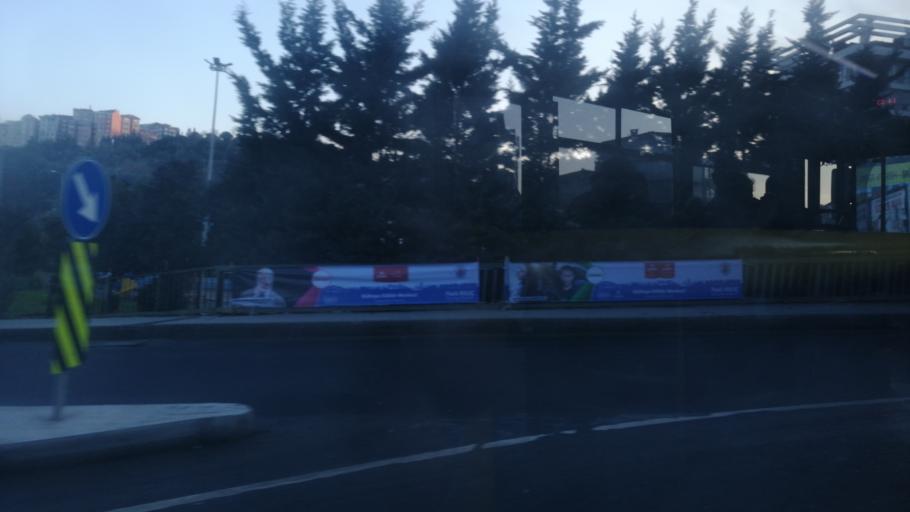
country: TR
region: Istanbul
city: Sisli
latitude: 41.0883
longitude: 28.9842
